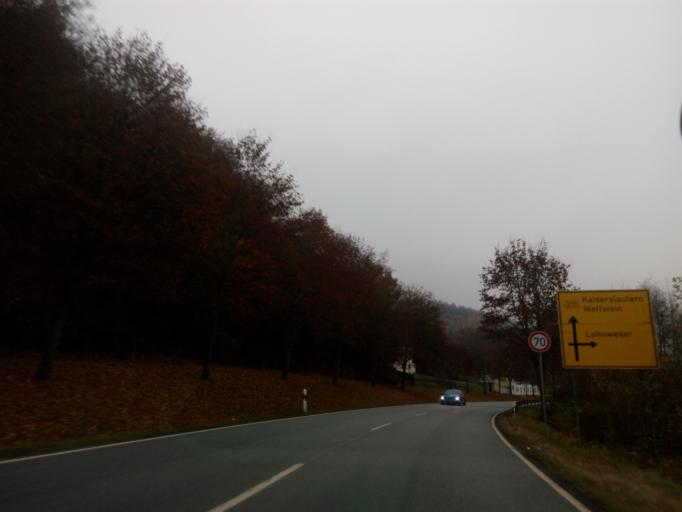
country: DE
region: Rheinland-Pfalz
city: Lohnweiler
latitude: 49.6388
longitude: 7.6003
